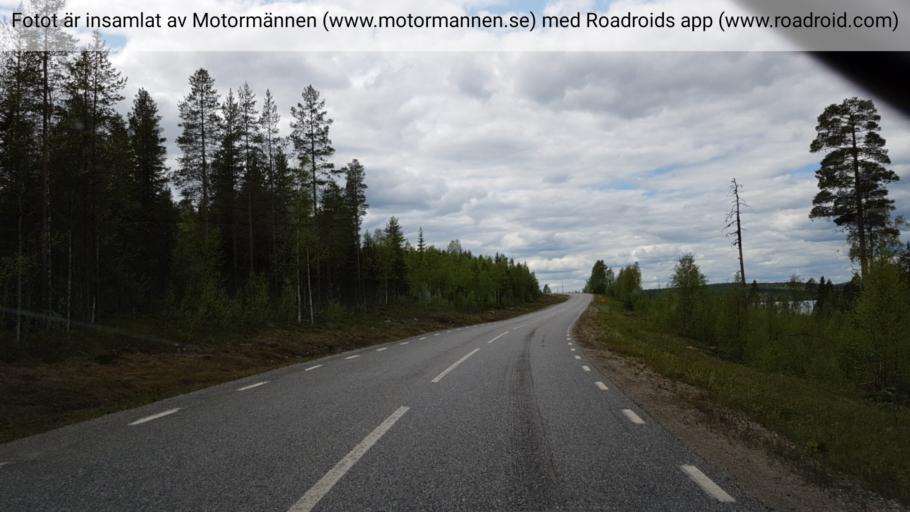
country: SE
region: Vaesterbotten
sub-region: Skelleftea Kommun
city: Langsele
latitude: 64.7549
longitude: 19.9500
